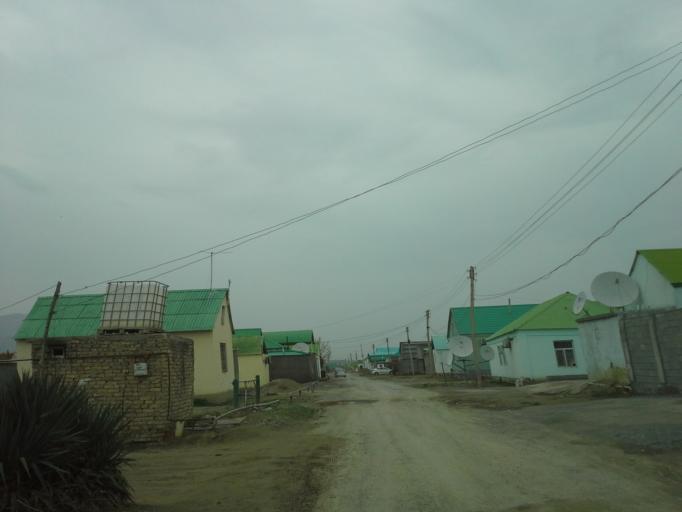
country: TM
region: Ahal
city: Abadan
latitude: 37.9701
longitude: 58.2296
